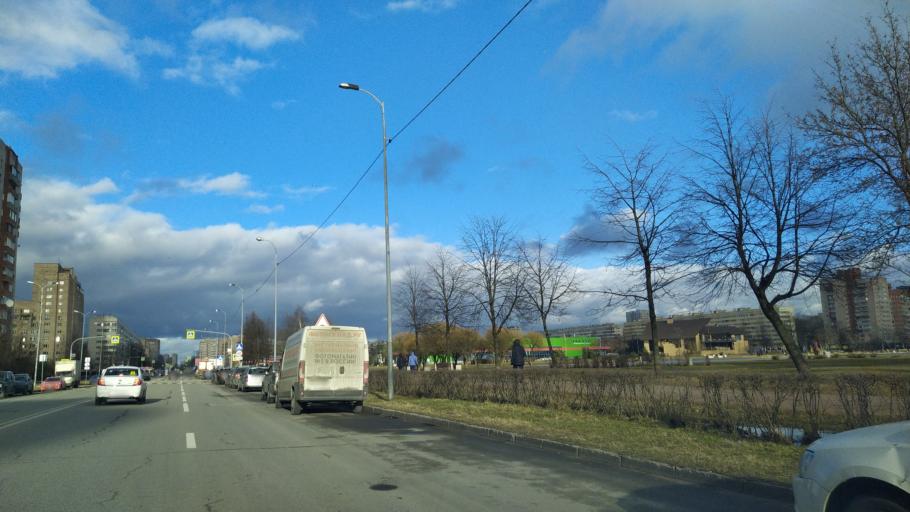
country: RU
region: St.-Petersburg
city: Grazhdanka
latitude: 60.0401
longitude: 30.3847
